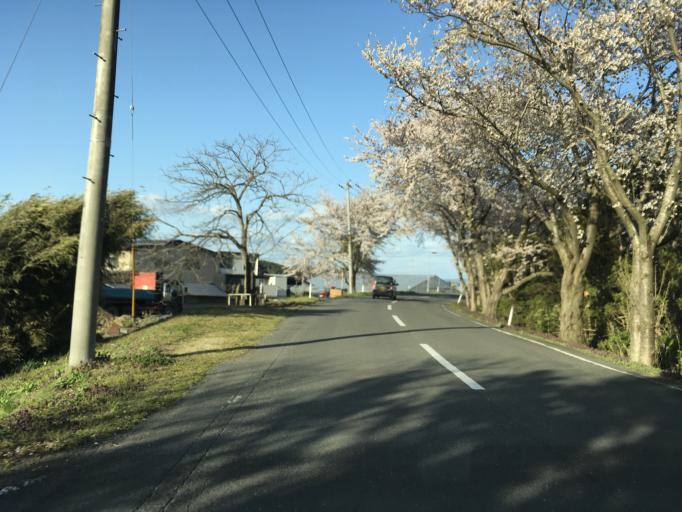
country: JP
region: Miyagi
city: Wakuya
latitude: 38.6467
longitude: 141.1760
